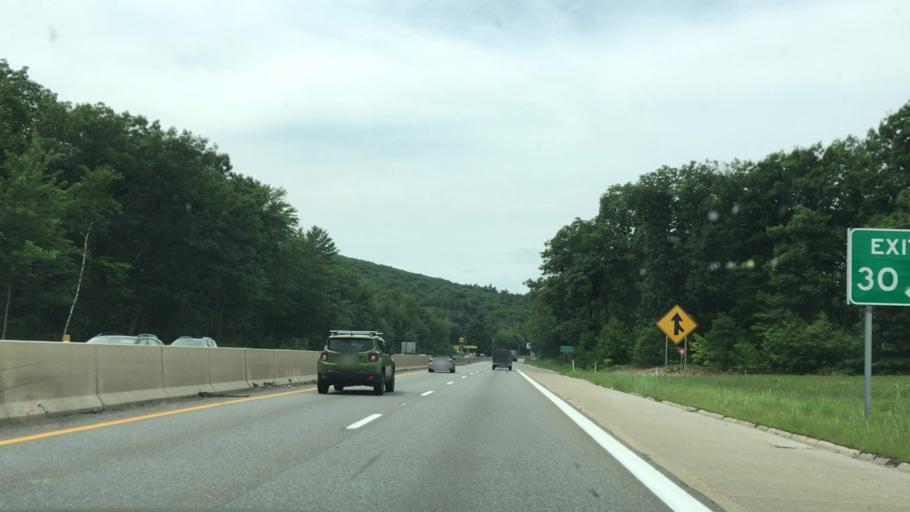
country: US
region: Massachusetts
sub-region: Worcester County
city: Leominster
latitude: 42.5515
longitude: -71.7843
